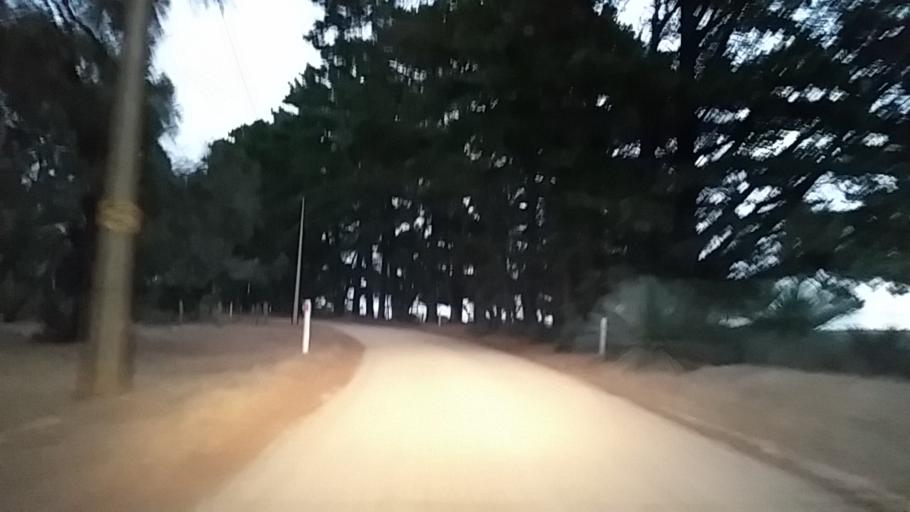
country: AU
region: South Australia
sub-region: Yankalilla
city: Normanville
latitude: -35.6309
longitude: 138.1937
